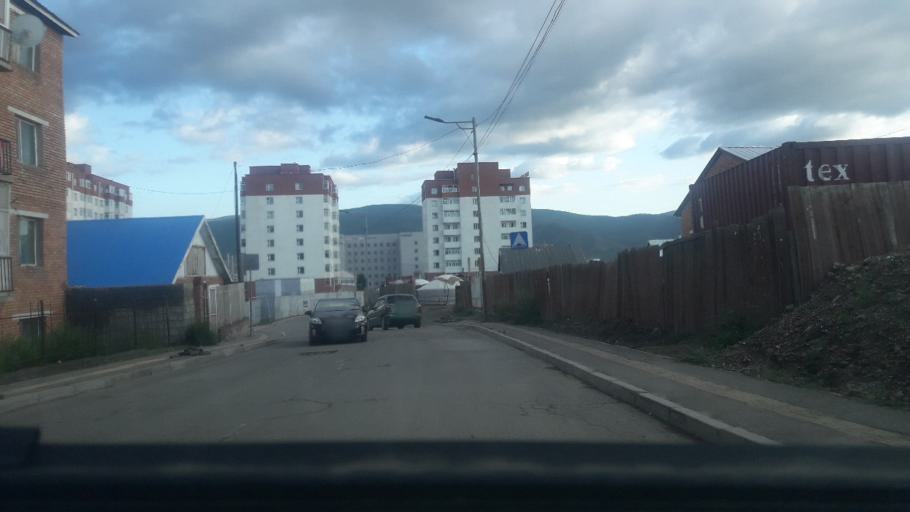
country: MN
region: Ulaanbaatar
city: Ulaanbaatar
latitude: 47.9187
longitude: 106.9954
